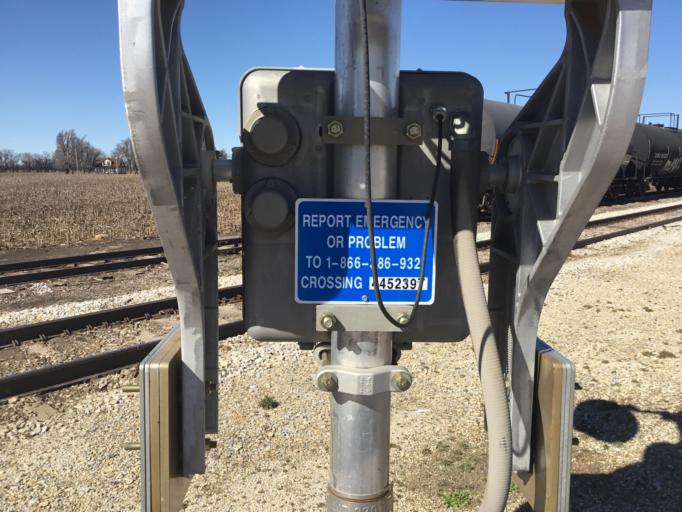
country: US
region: Kansas
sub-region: Reno County
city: Haven
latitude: 37.8633
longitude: -97.6654
